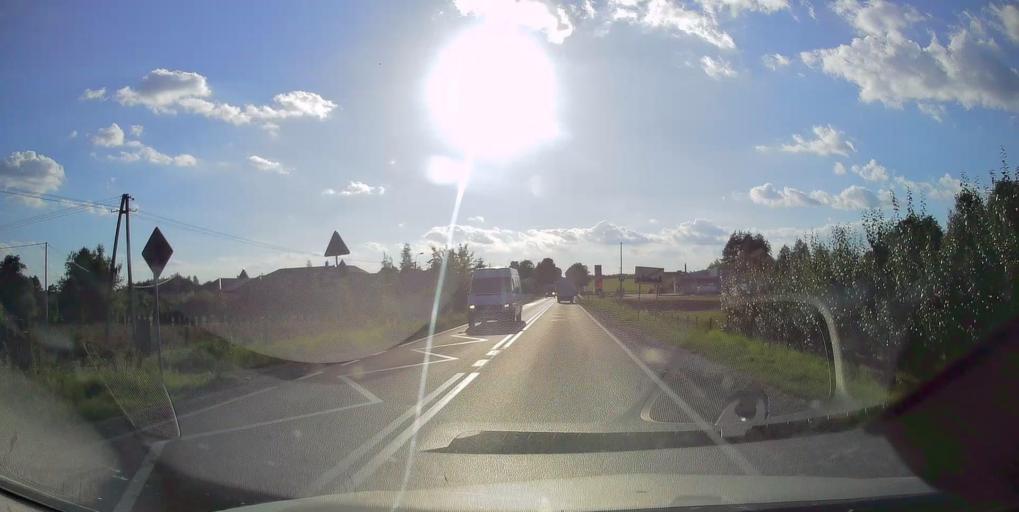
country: PL
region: Masovian Voivodeship
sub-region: Powiat grojecki
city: Bledow
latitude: 51.8000
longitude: 20.6194
